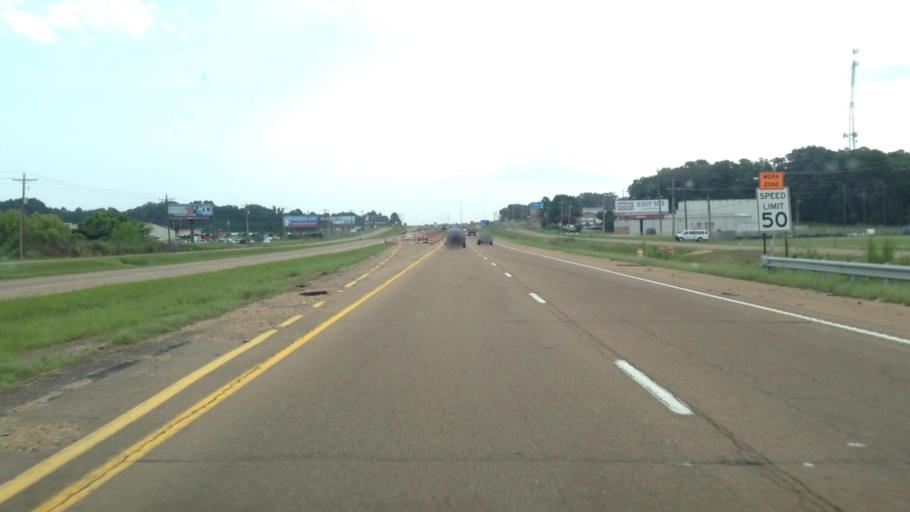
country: US
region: Mississippi
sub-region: Hinds County
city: Byram
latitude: 32.1704
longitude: -90.2657
